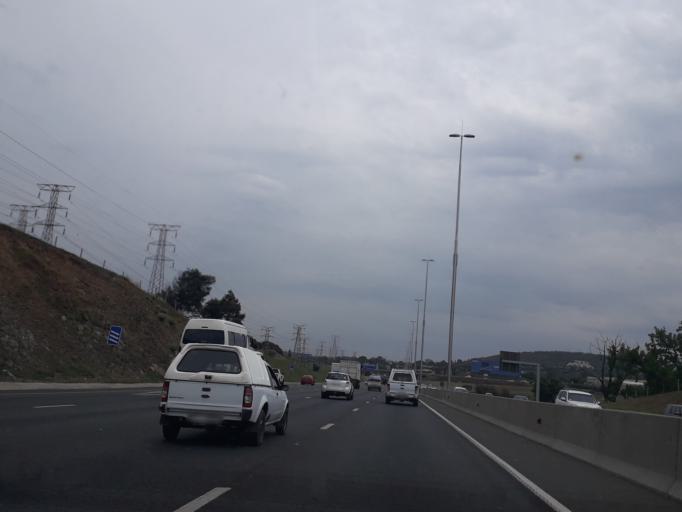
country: ZA
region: Gauteng
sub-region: City of Johannesburg Metropolitan Municipality
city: Modderfontein
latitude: -26.1414
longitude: 28.1322
